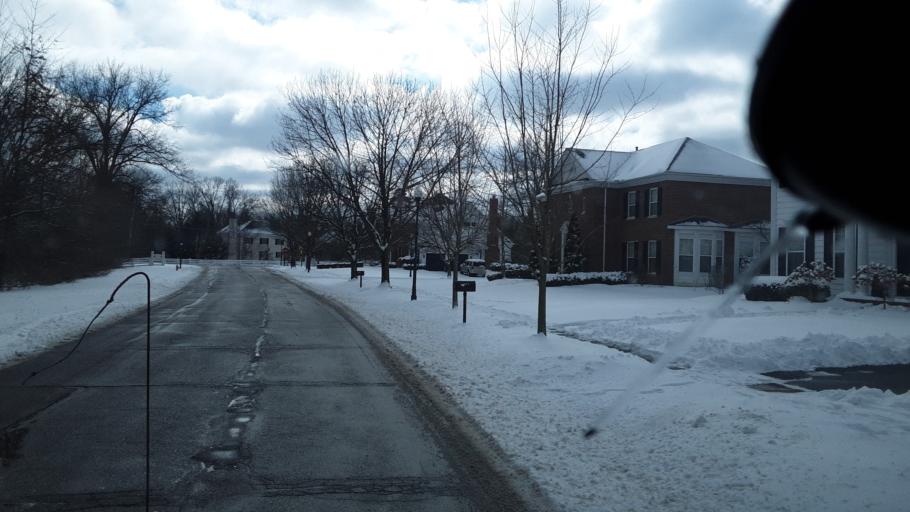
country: US
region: Ohio
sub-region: Franklin County
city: New Albany
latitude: 40.0822
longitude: -82.8265
